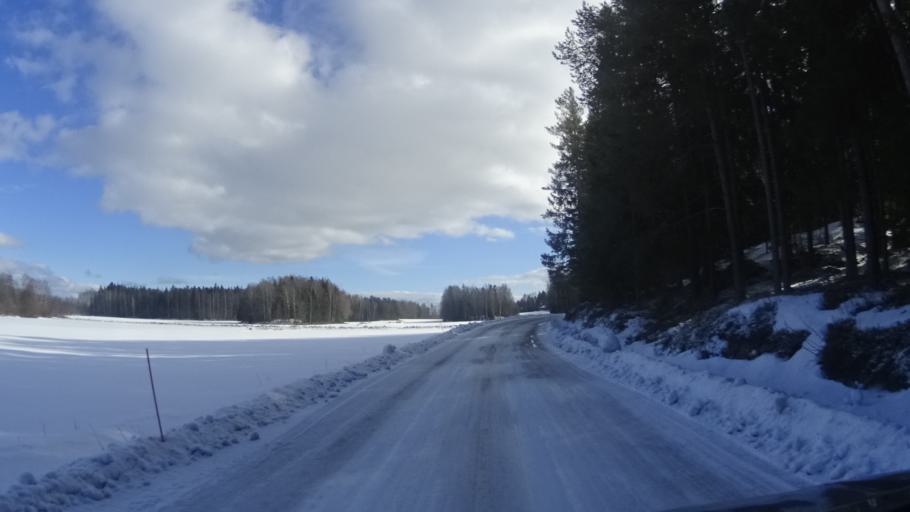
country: FI
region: Uusimaa
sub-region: Helsinki
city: Vantaa
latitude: 60.2441
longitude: 25.1761
